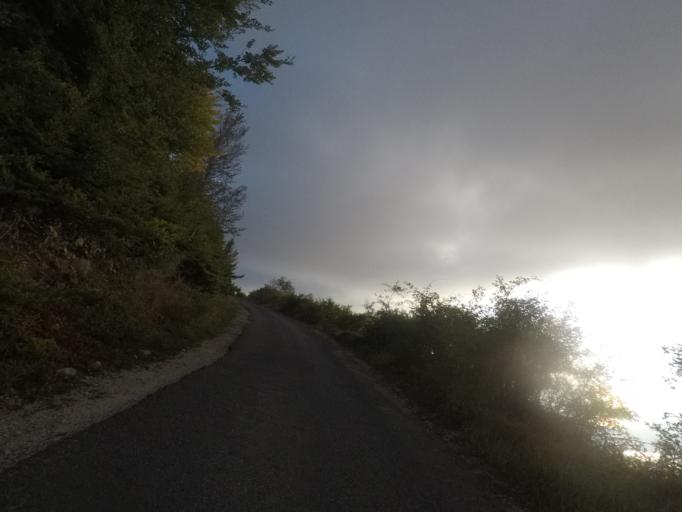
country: ME
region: Kotor
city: Kotor
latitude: 42.4113
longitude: 18.7964
